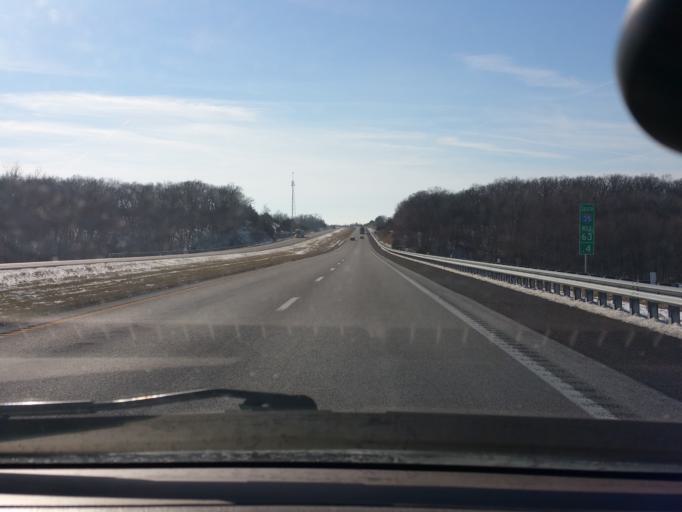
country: US
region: Missouri
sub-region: Clinton County
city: Cameron
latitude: 39.8794
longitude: -94.1638
